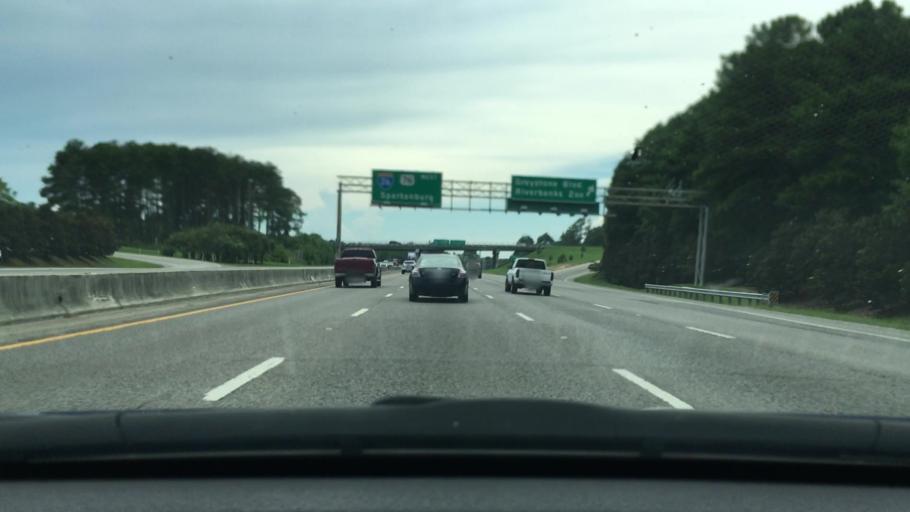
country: US
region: South Carolina
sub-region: Lexington County
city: West Columbia
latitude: 34.0123
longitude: -81.0724
